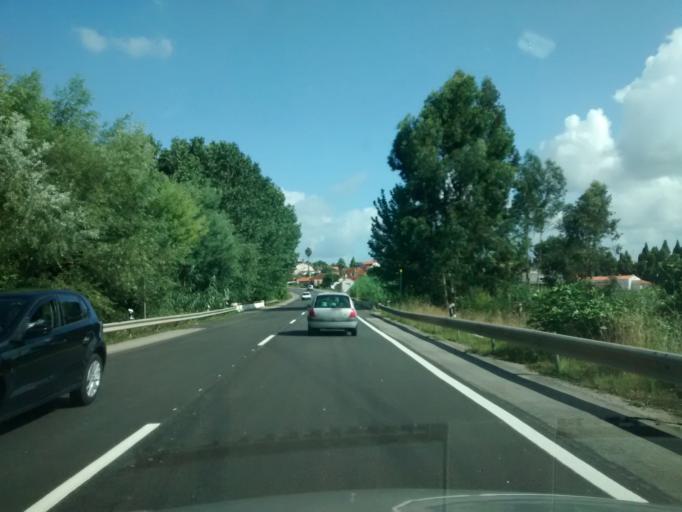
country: PT
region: Aveiro
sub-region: Oliveira do Bairro
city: Oliveira do Bairro
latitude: 40.5297
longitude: -8.5084
